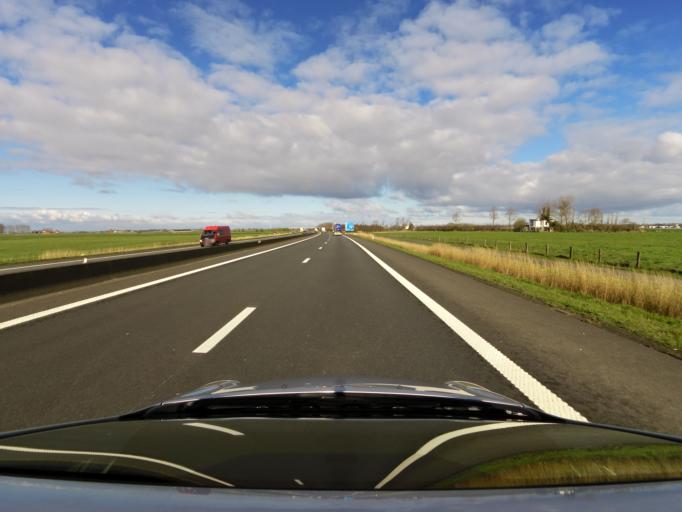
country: BE
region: Flanders
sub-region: Provincie West-Vlaanderen
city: Veurne
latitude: 51.0649
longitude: 2.6356
